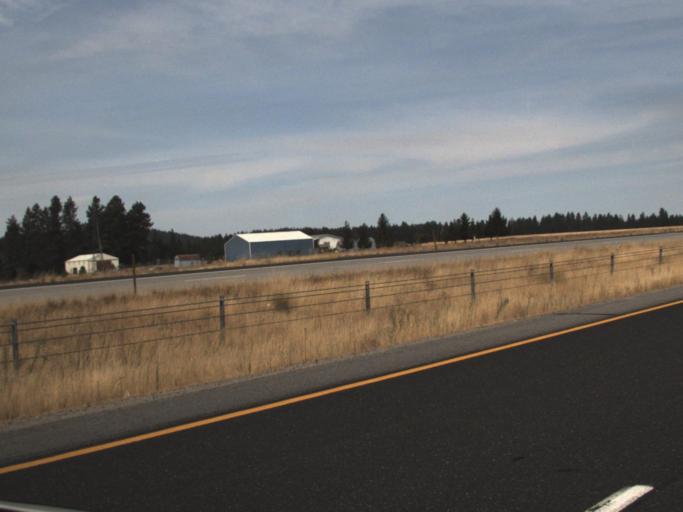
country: US
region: Washington
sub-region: Spokane County
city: Fairwood
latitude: 47.8367
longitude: -117.4215
